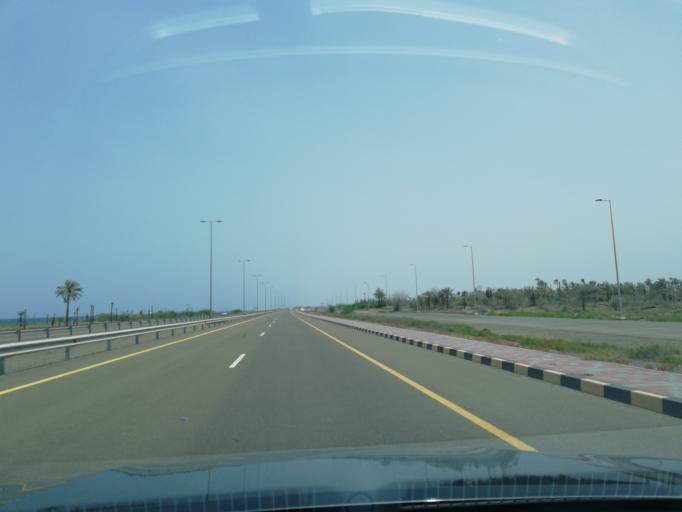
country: OM
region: Al Batinah
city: Al Liwa'
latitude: 24.6340
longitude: 56.5252
